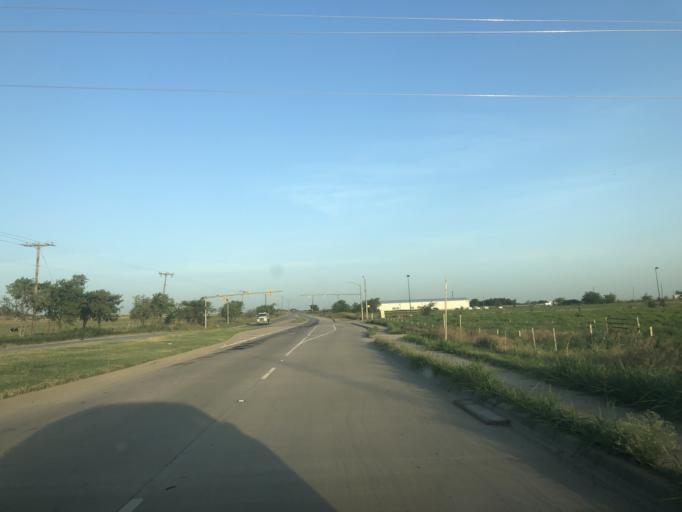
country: US
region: Texas
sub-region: Tarrant County
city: White Settlement
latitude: 32.7745
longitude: -97.4796
